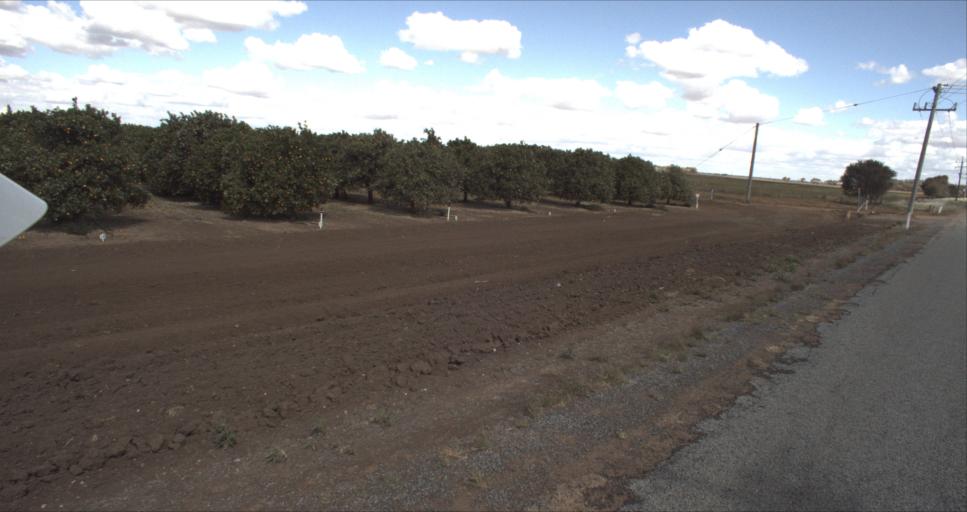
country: AU
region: New South Wales
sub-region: Leeton
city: Leeton
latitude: -34.5240
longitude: 146.2222
